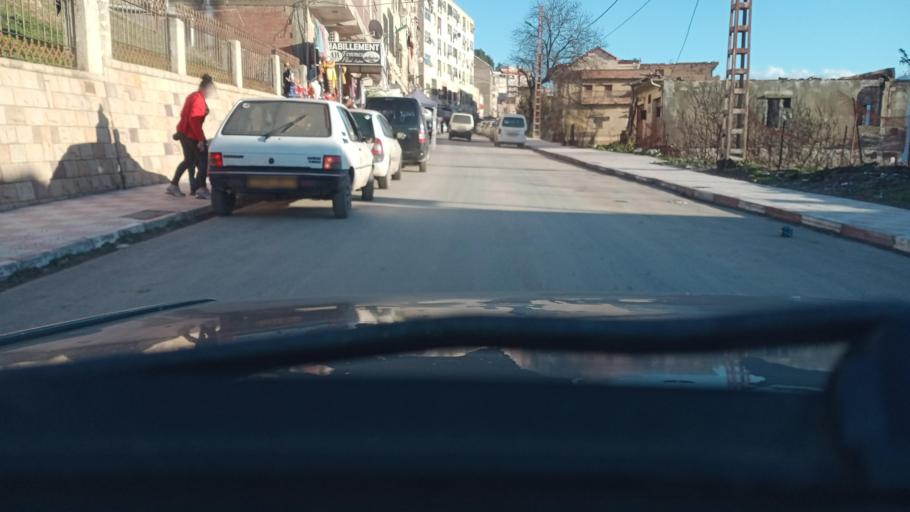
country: DZ
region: Tizi Ouzou
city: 'Ain el Hammam
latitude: 36.5746
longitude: 4.3050
